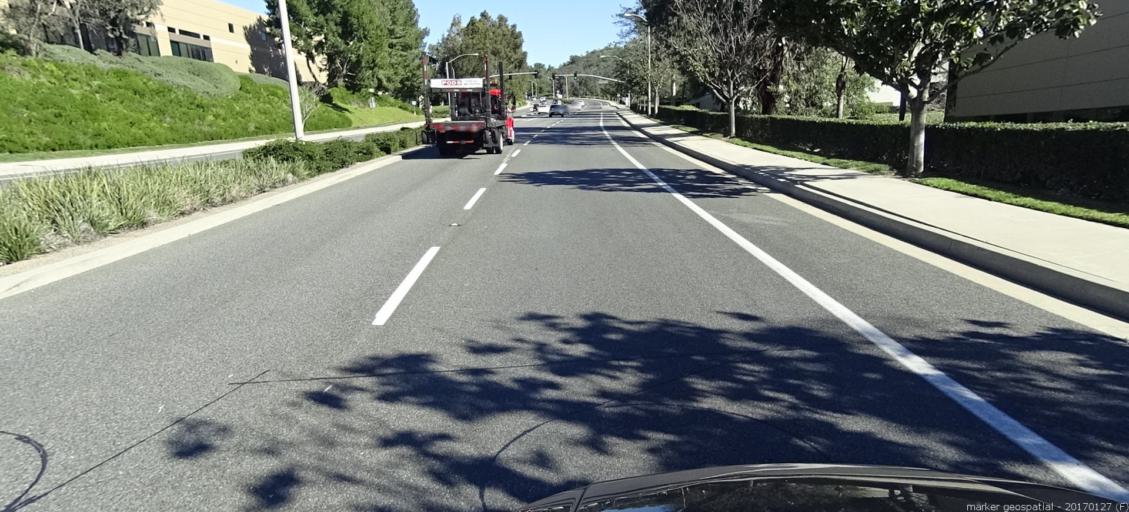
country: US
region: California
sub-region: Orange County
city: Lake Forest
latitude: 33.6617
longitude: -117.6947
